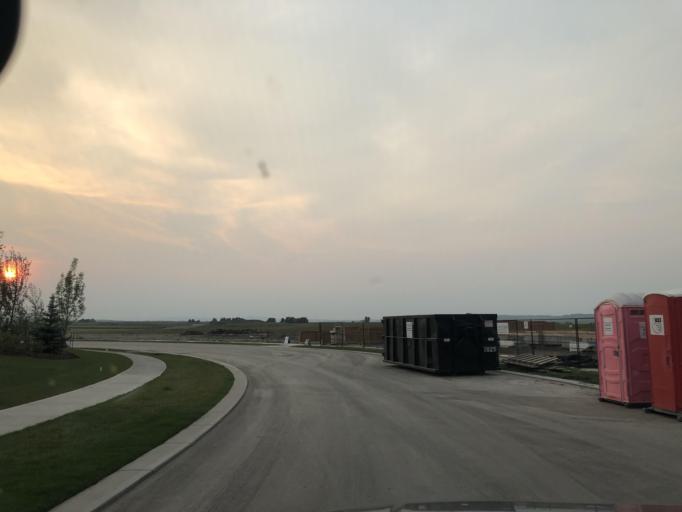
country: CA
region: Alberta
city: Cochrane
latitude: 51.1217
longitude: -114.3916
